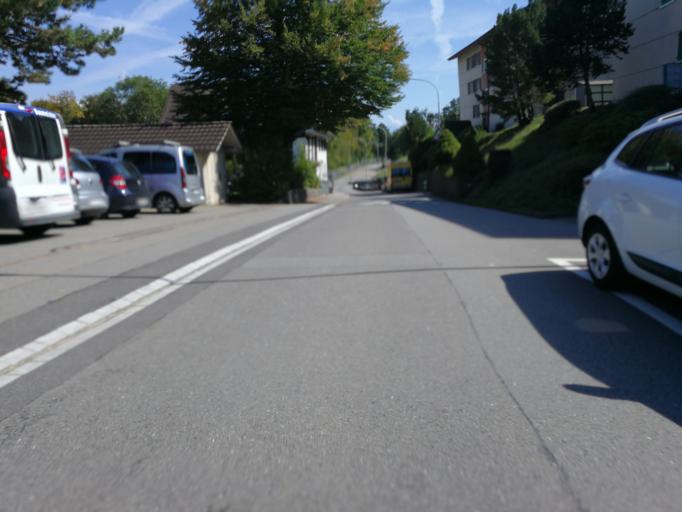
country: CH
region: Zurich
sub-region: Bezirk Horgen
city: Au / Mittel-Dorf
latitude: 47.2448
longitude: 8.6462
